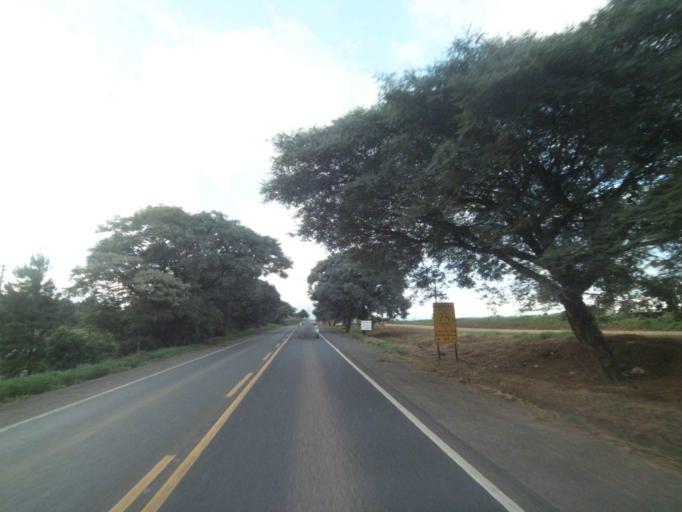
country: BR
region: Parana
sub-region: Telemaco Borba
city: Telemaco Borba
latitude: -24.3503
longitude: -50.6606
